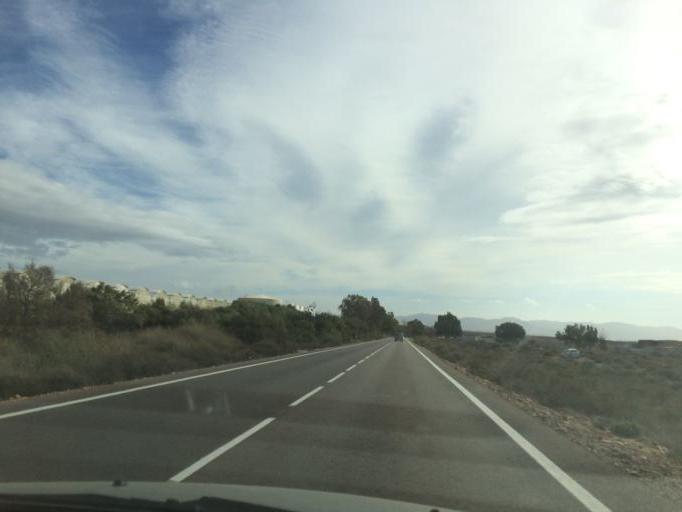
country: ES
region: Andalusia
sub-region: Provincia de Almeria
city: Retamar
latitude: 36.8379
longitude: -2.2914
